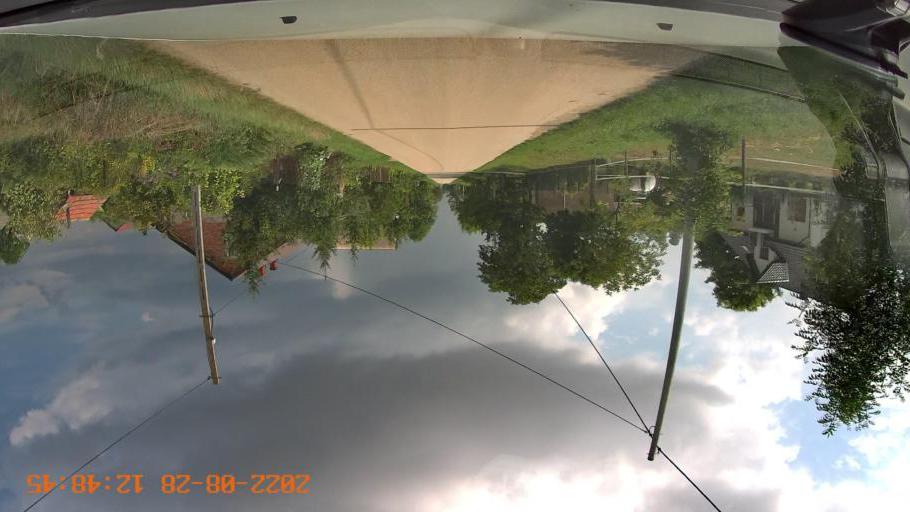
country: PL
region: Swietokrzyskie
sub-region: Powiat pinczowski
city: Dzialoszyce
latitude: 50.3584
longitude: 20.2880
